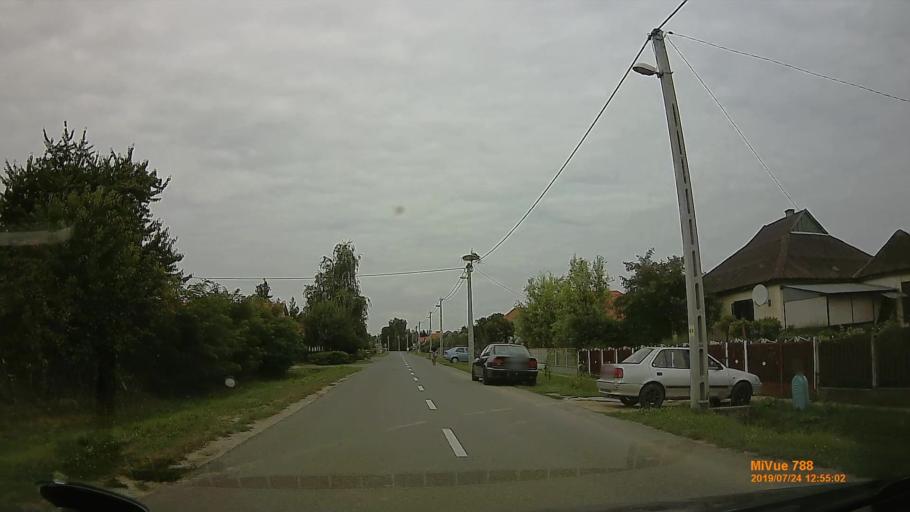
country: HU
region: Szabolcs-Szatmar-Bereg
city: Aranyosapati
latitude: 48.2215
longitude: 22.2940
